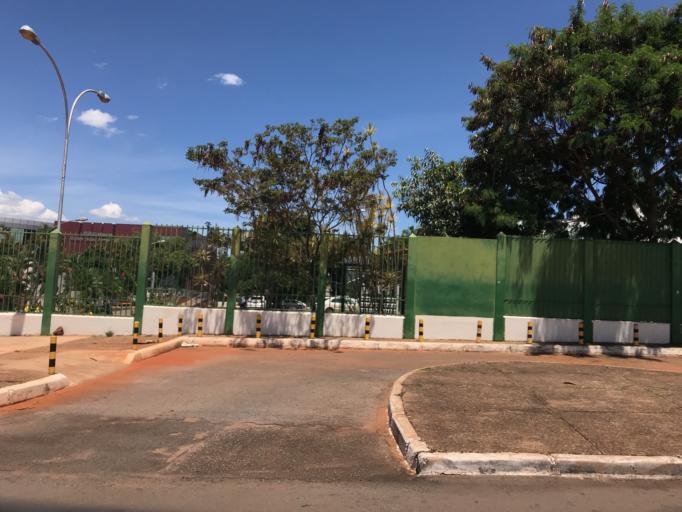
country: BR
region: Federal District
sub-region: Brasilia
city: Brasilia
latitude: -15.7681
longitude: -47.8941
